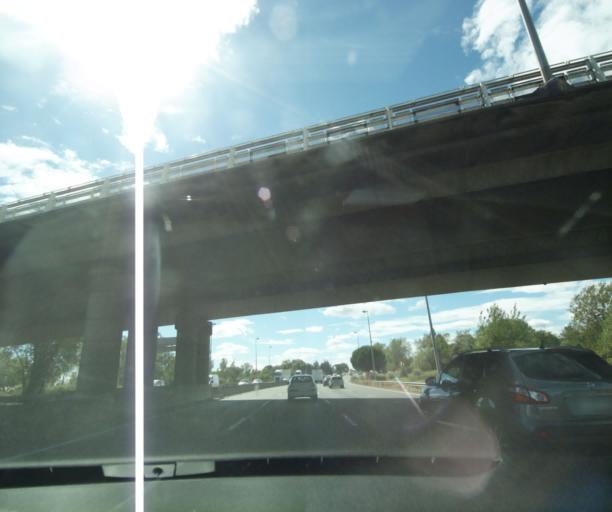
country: FR
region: Aquitaine
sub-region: Departement de la Gironde
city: Bouliac
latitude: 44.8118
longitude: -0.5219
